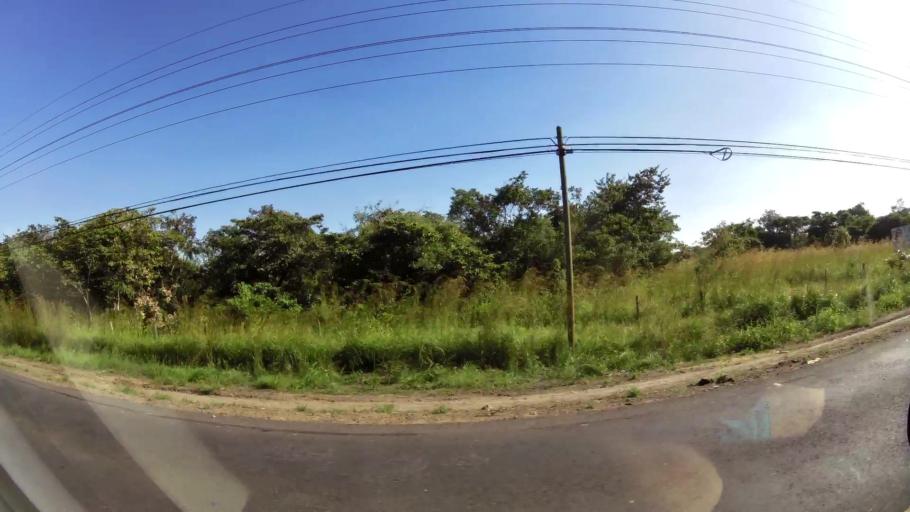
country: CR
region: Guanacaste
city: Liberia
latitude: 10.6015
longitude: -85.5171
